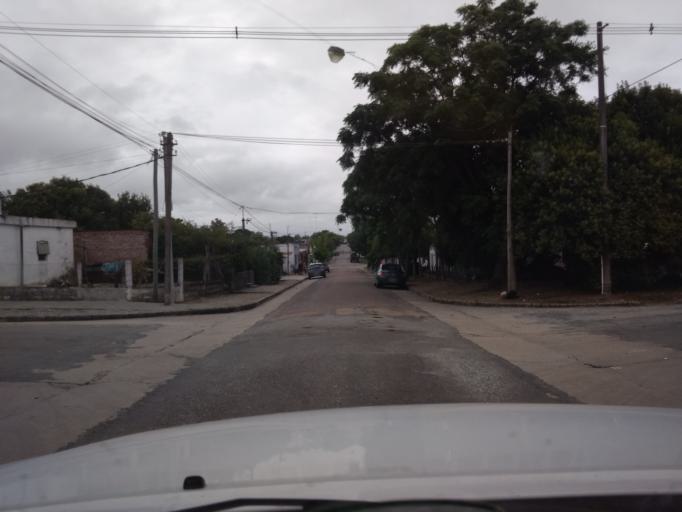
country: UY
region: Florida
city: Florida
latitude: -34.1052
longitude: -56.2101
